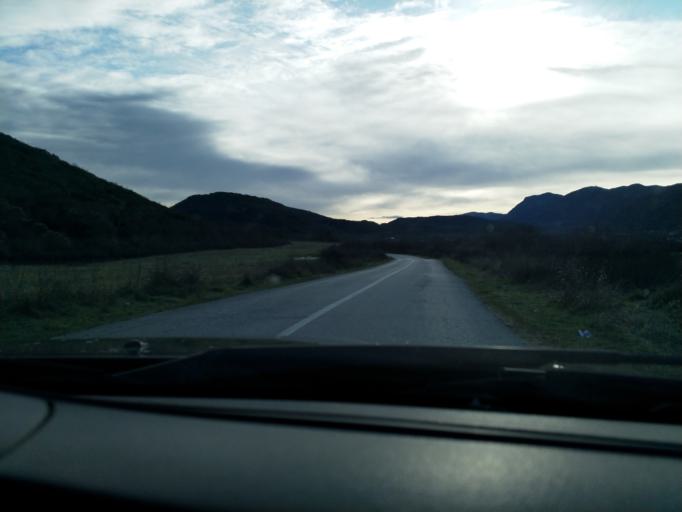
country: GR
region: Epirus
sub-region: Nomos Ioanninon
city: Asprangeloi
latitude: 39.8702
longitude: 20.7097
